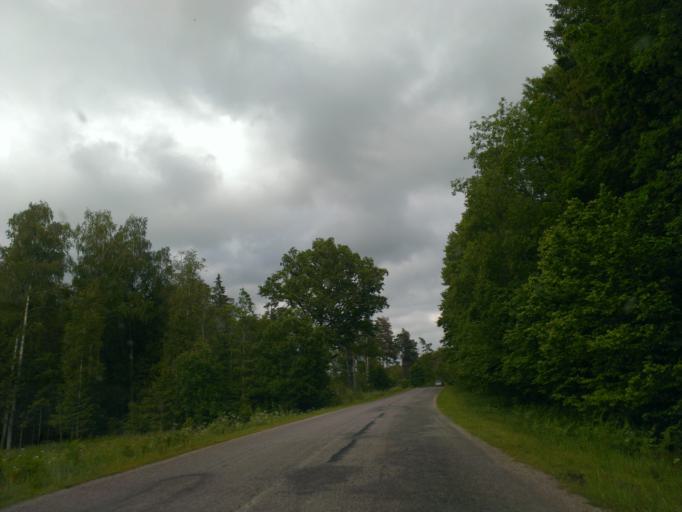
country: LV
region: Skrunda
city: Skrunda
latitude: 56.6939
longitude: 21.8533
